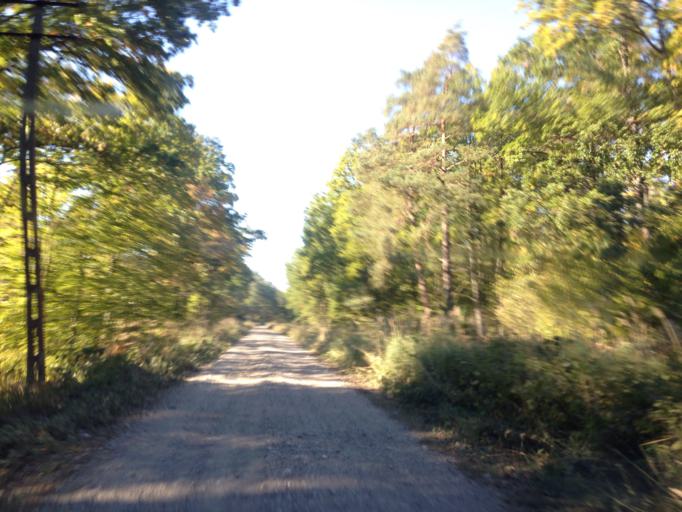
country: PL
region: Kujawsko-Pomorskie
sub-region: Powiat brodnicki
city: Gorzno
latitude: 53.2388
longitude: 19.6878
